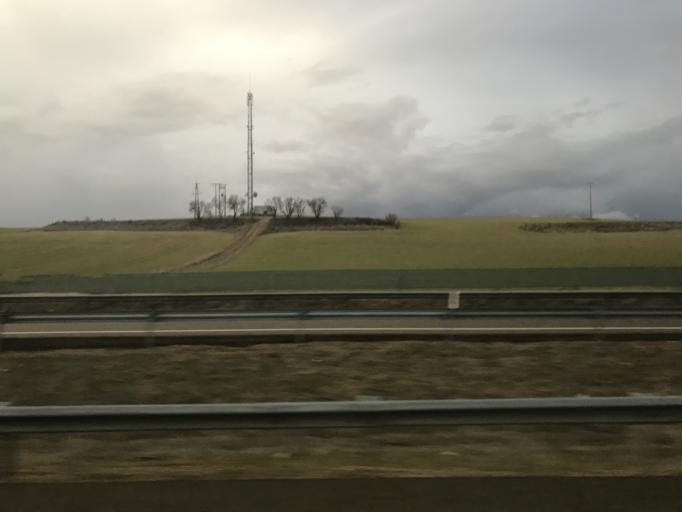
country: ES
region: Castille and Leon
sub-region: Provincia de Palencia
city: Torquemada
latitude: 42.0132
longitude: -4.3499
